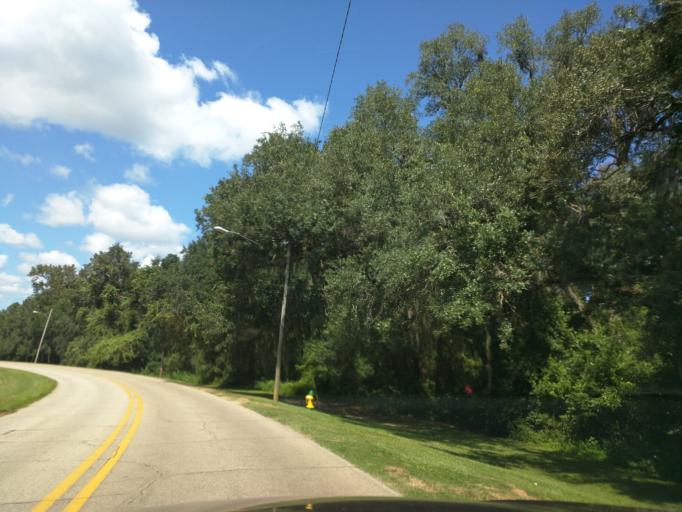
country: US
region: Florida
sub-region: Leon County
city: Tallahassee
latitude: 30.4494
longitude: -84.2161
